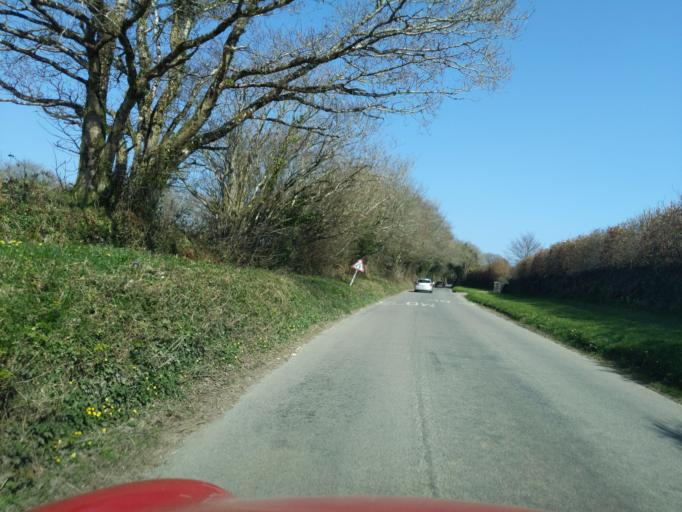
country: GB
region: England
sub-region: Devon
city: Horrabridge
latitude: 50.4883
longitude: -4.1185
